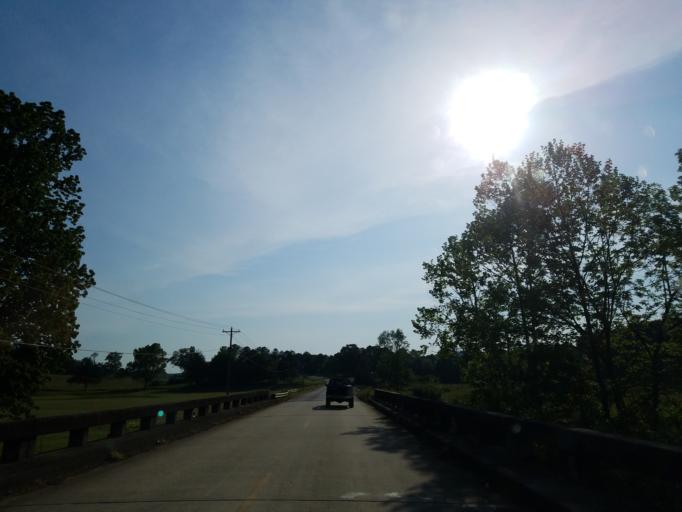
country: US
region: Georgia
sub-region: Chattooga County
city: Trion
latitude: 34.5689
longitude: -85.1608
